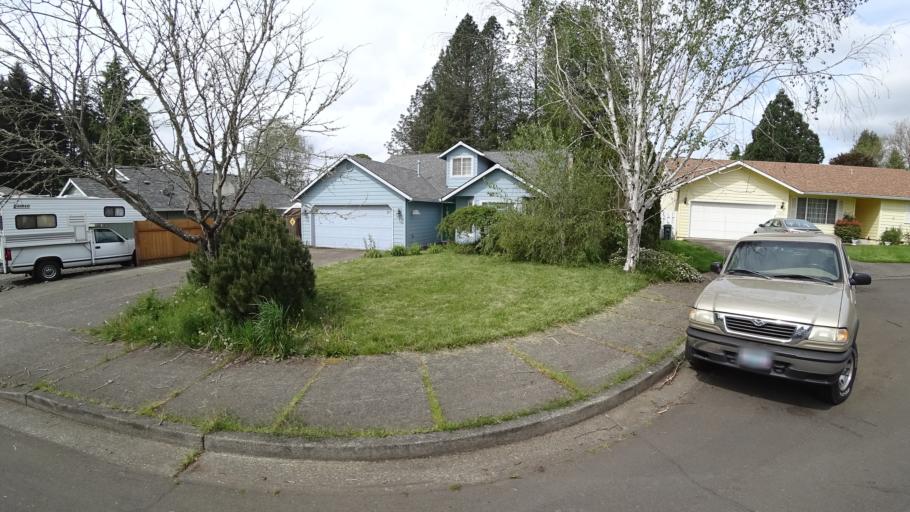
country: US
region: Oregon
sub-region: Washington County
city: Hillsboro
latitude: 45.5260
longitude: -123.0004
